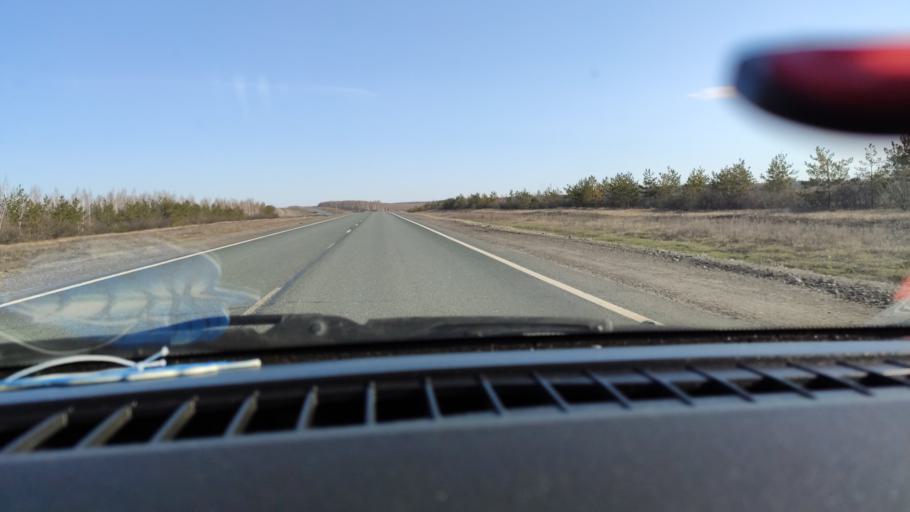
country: RU
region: Samara
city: Syzran'
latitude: 52.8818
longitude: 48.2925
